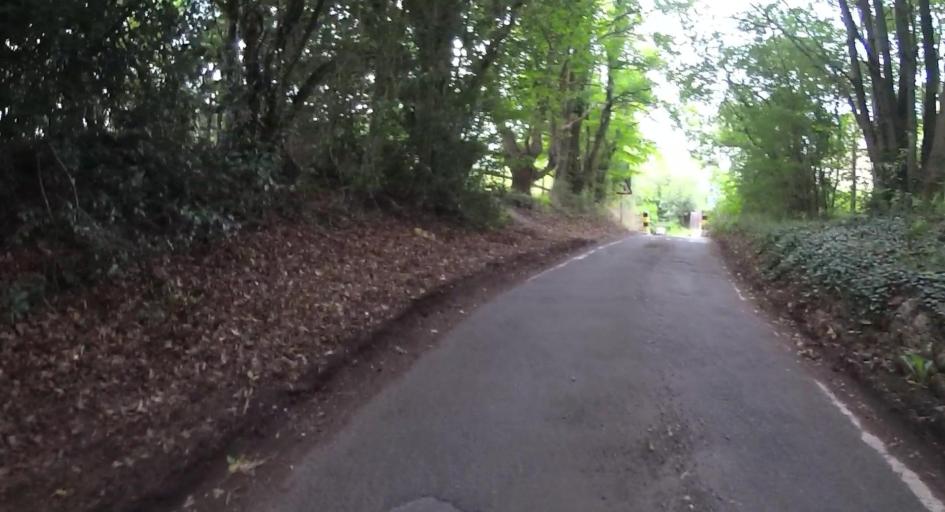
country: GB
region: England
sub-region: Surrey
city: Knaphill
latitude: 51.3265
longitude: -0.6227
